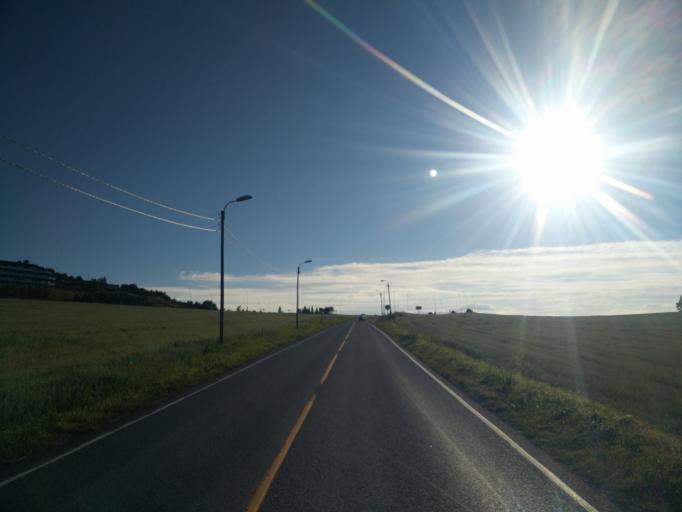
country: NO
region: Sor-Trondelag
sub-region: Malvik
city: Malvik
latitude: 63.4257
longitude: 10.5517
